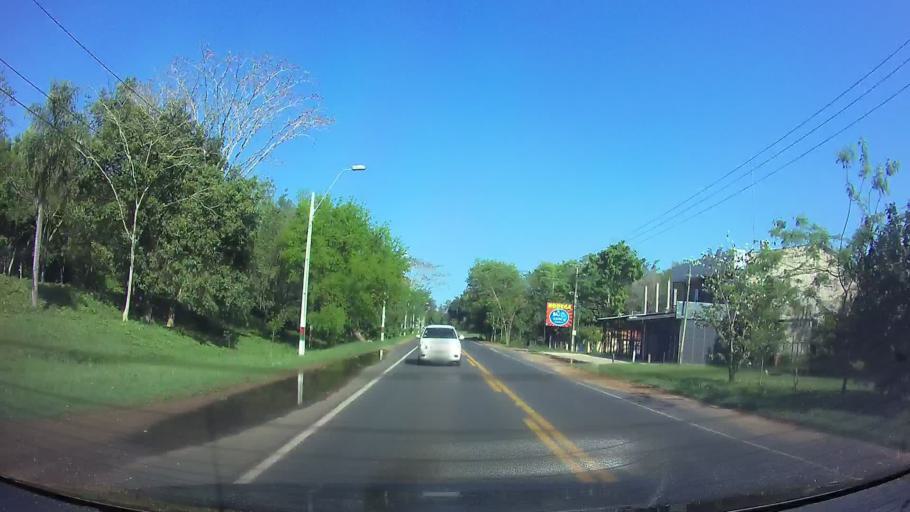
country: PY
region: Central
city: Aregua
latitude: -25.3216
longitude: -57.3688
